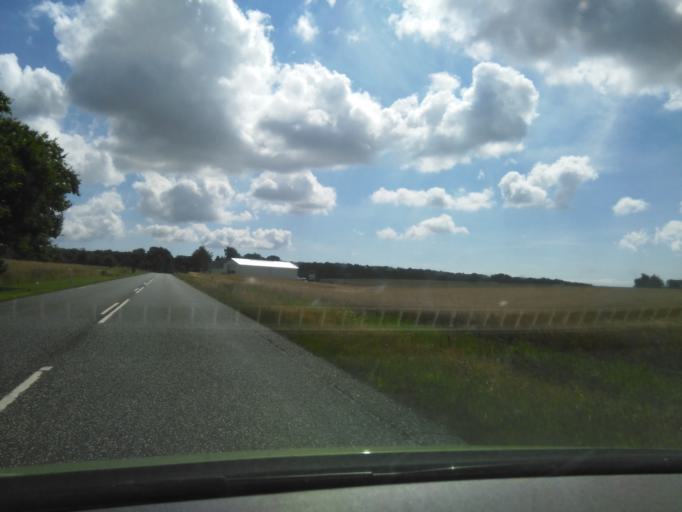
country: DK
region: Central Jutland
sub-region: Arhus Kommune
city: Solbjerg
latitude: 55.9715
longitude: 10.0662
